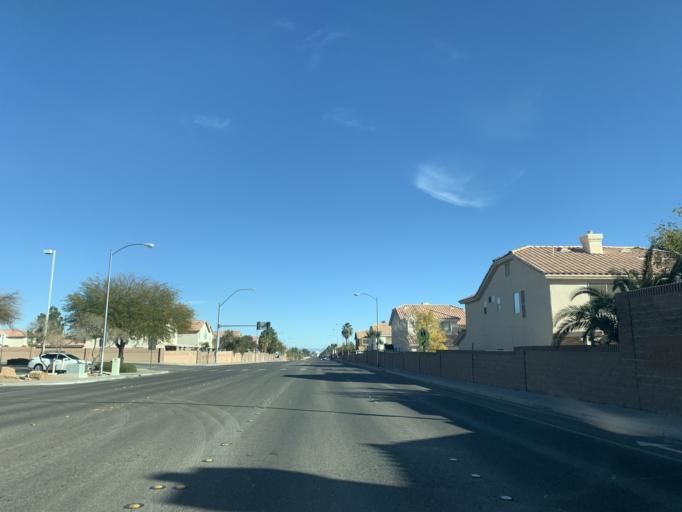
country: US
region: Nevada
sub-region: Clark County
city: Summerlin South
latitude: 36.1224
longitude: -115.3023
